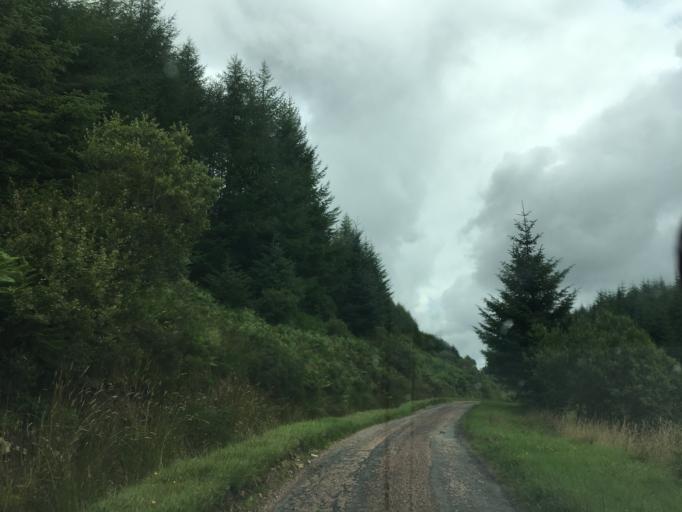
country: GB
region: Scotland
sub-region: Argyll and Bute
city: Oban
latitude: 56.2513
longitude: -5.4163
